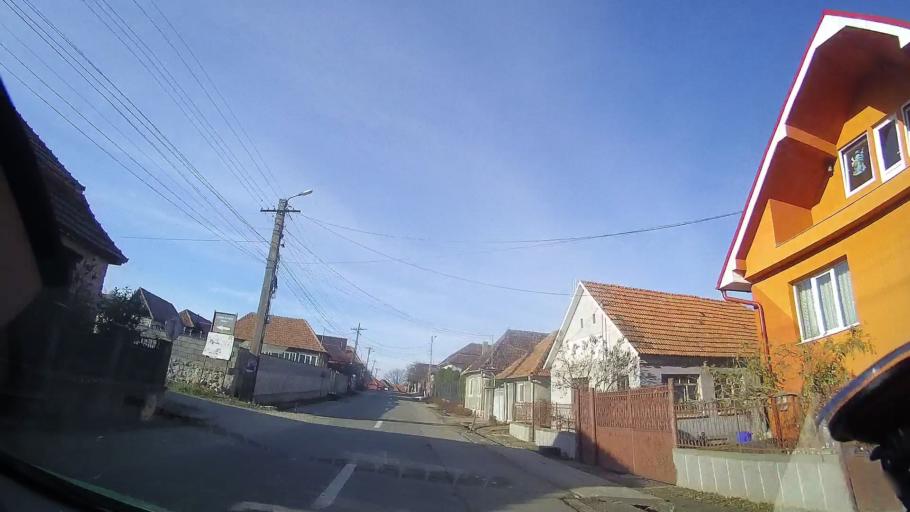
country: RO
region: Bihor
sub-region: Comuna Magesti
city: Magesti
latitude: 47.0095
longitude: 22.4496
